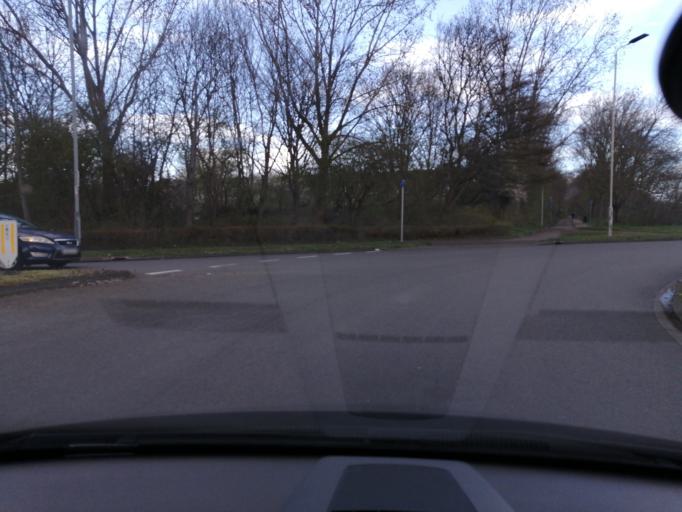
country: GB
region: England
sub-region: Peterborough
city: Peterborough
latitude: 52.5844
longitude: -0.2659
